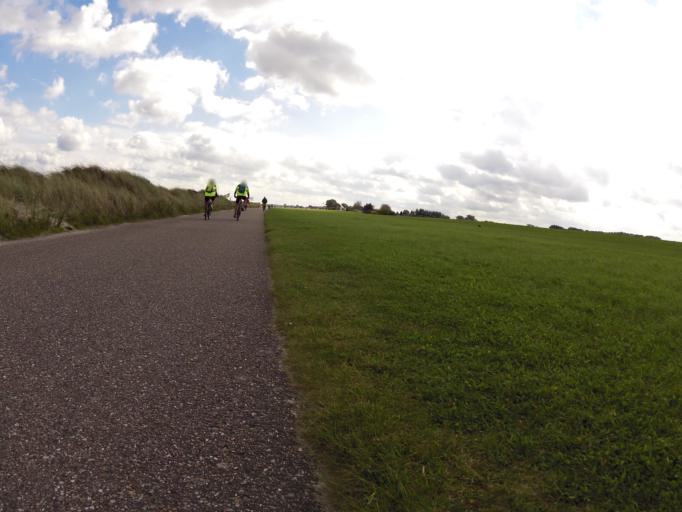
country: DE
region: Schleswig-Holstein
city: Krummbek
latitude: 54.4221
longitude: 10.3988
